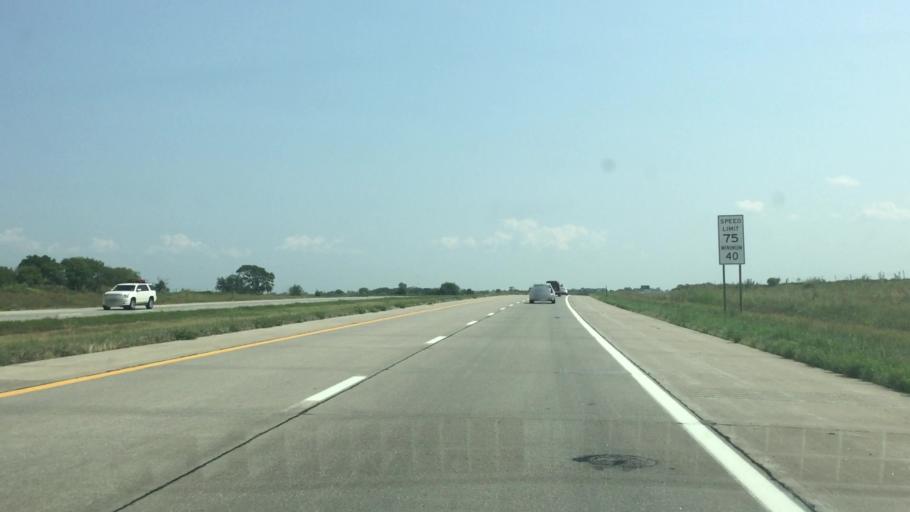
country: US
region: Kansas
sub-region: Franklin County
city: Ottawa
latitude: 38.4947
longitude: -95.4638
